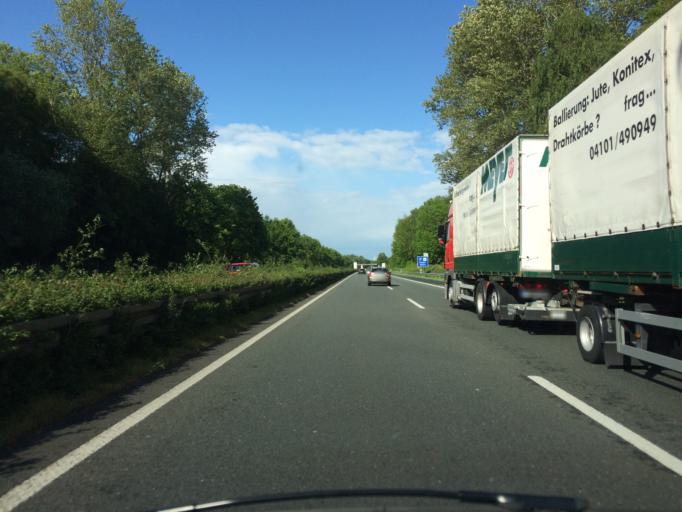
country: DE
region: North Rhine-Westphalia
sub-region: Regierungsbezirk Munster
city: Dulmen
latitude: 51.8605
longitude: 7.3056
